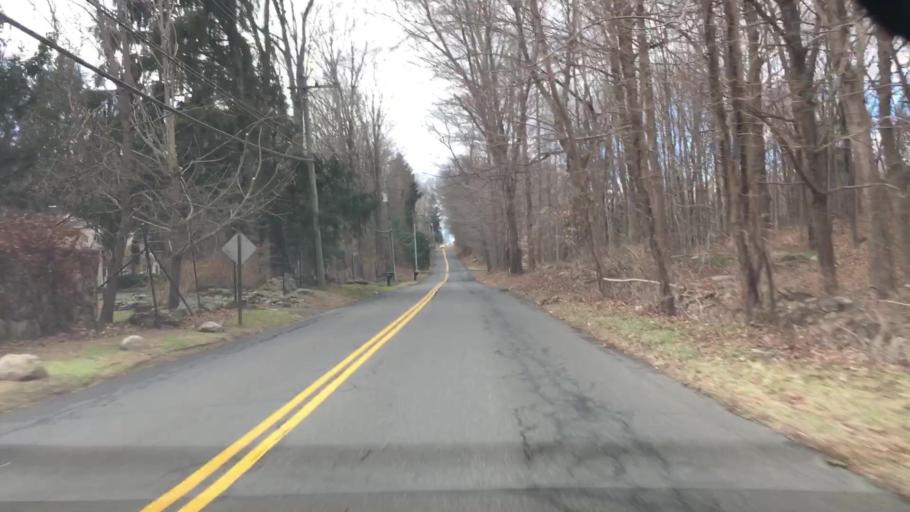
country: US
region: Connecticut
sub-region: Fairfield County
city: Danbury
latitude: 41.3627
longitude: -73.5105
